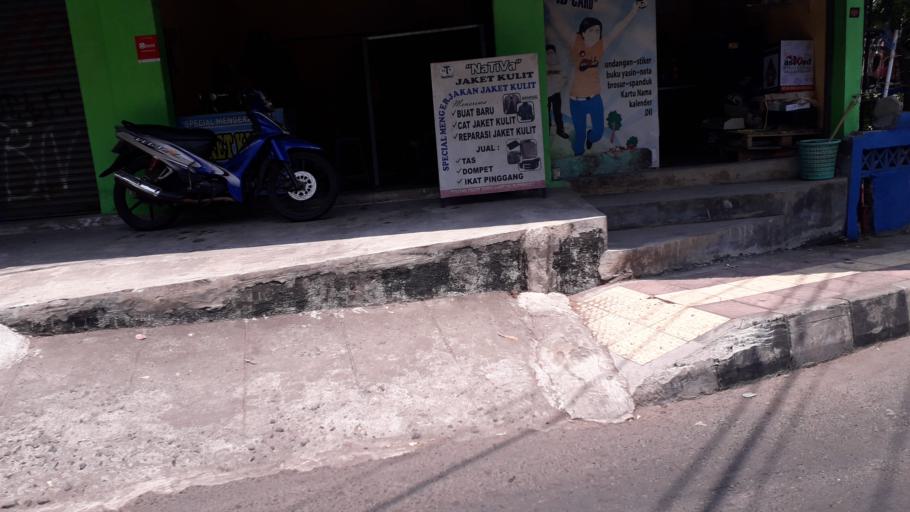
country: ID
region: Daerah Istimewa Yogyakarta
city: Yogyakarta
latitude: -7.7882
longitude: 110.3577
